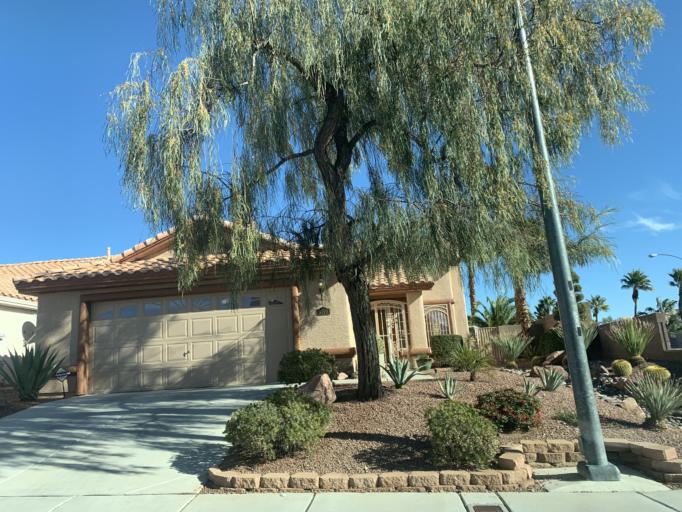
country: US
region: Nevada
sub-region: Clark County
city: Summerlin South
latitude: 36.1207
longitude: -115.3018
